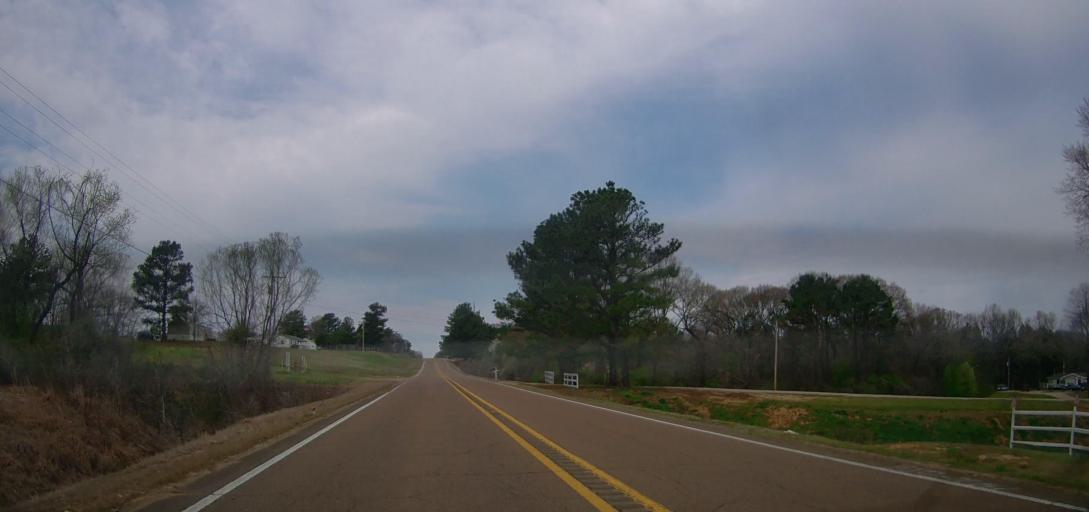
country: US
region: Mississippi
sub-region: Marshall County
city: Byhalia
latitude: 34.8390
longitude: -89.5968
